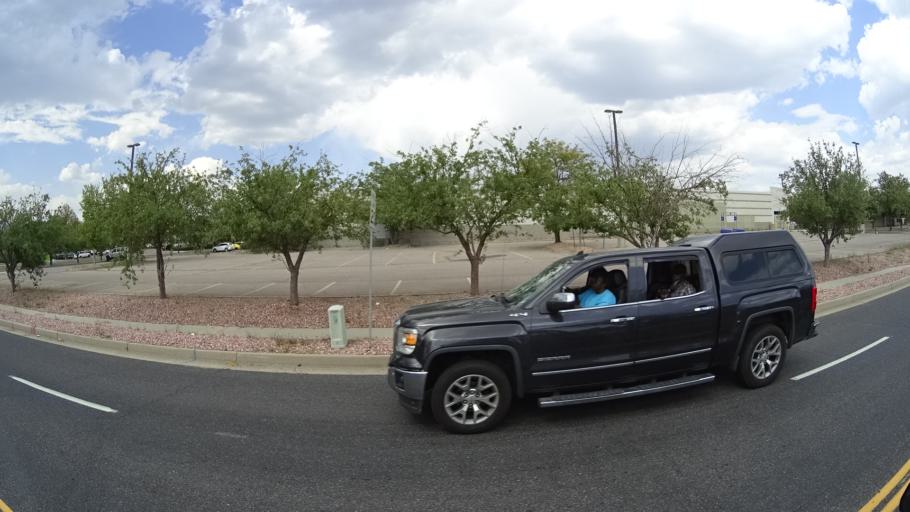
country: US
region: Colorado
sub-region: El Paso County
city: Cimarron Hills
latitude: 38.8458
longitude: -104.7592
